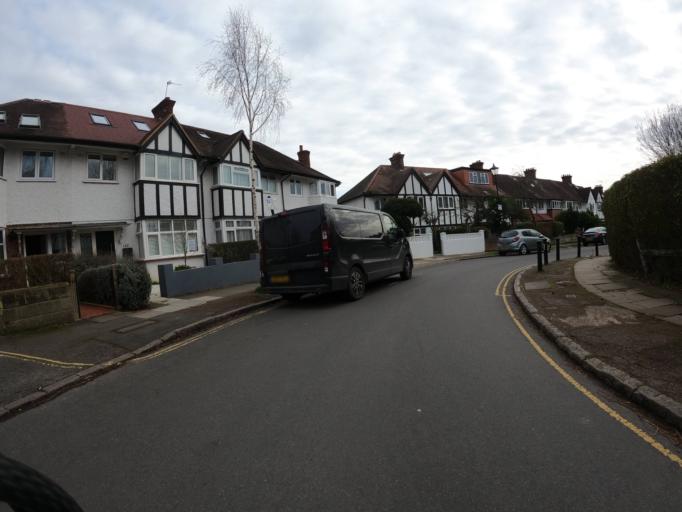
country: GB
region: England
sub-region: Greater London
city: Acton
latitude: 51.5011
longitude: -0.2805
